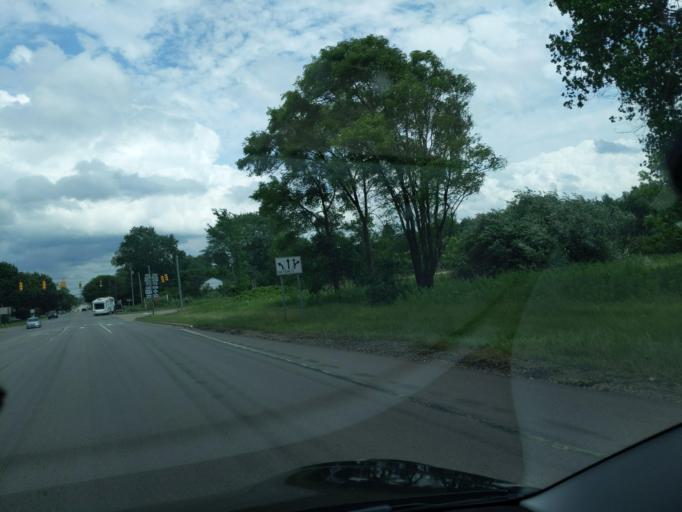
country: US
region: Michigan
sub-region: Jackson County
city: Jackson
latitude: 42.2911
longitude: -84.4320
